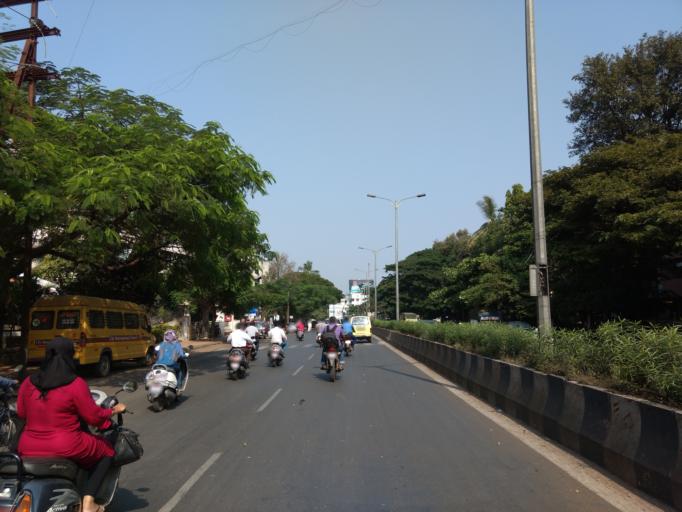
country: IN
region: Maharashtra
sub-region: Pune Division
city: Pune
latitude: 18.4797
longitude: 73.8614
